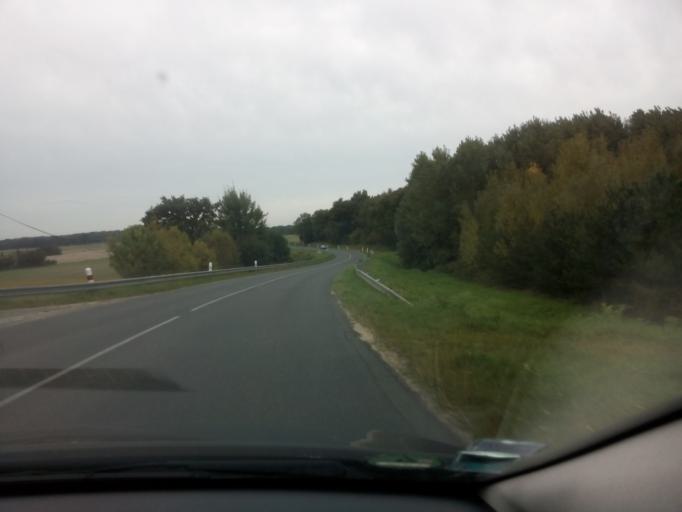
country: FR
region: Pays de la Loire
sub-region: Departement de Maine-et-Loire
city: Seiches-sur-le-Loir
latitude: 47.5562
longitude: -0.3339
